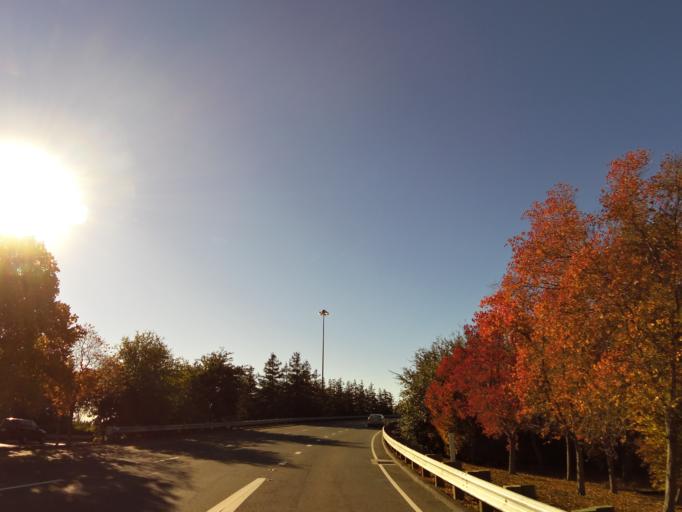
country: US
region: California
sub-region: Yolo County
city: West Sacramento
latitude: 38.6873
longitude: -121.5905
